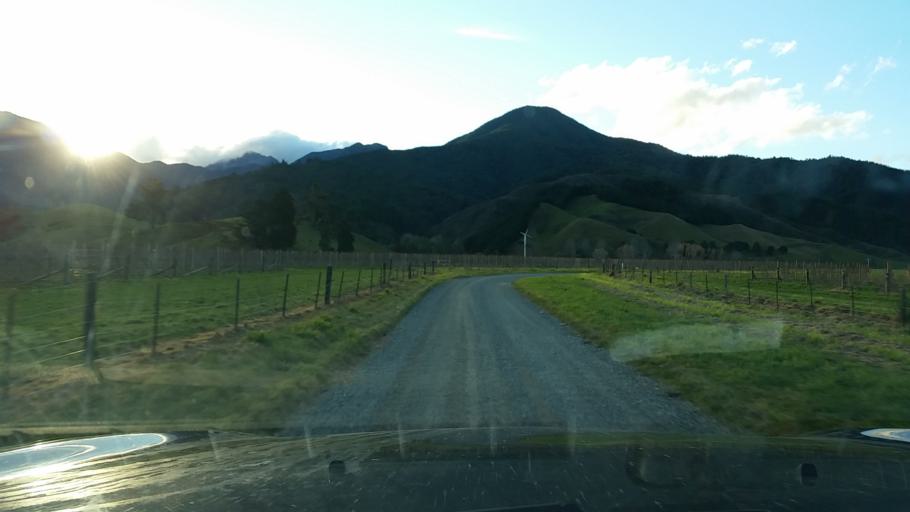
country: NZ
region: Marlborough
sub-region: Marlborough District
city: Blenheim
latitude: -41.5105
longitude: 173.5827
